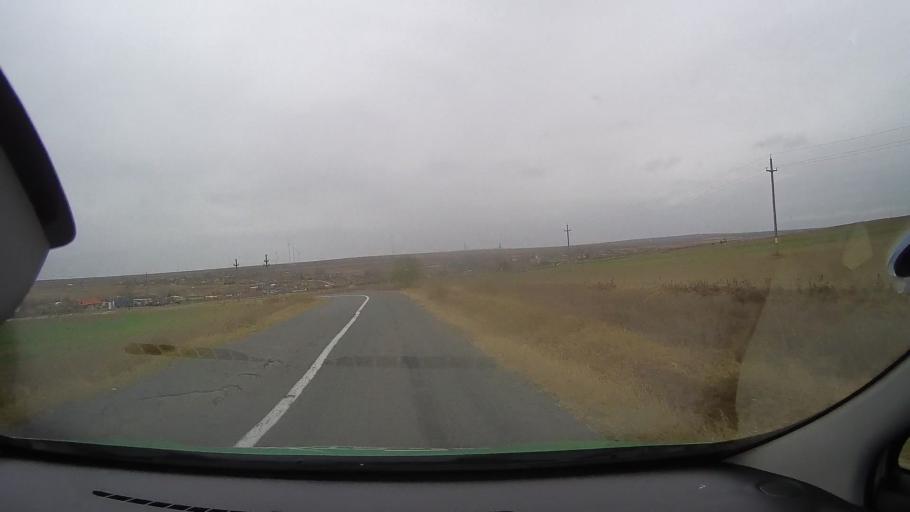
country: RO
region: Constanta
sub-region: Comuna Targusor
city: Targusor
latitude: 44.4883
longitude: 28.3645
